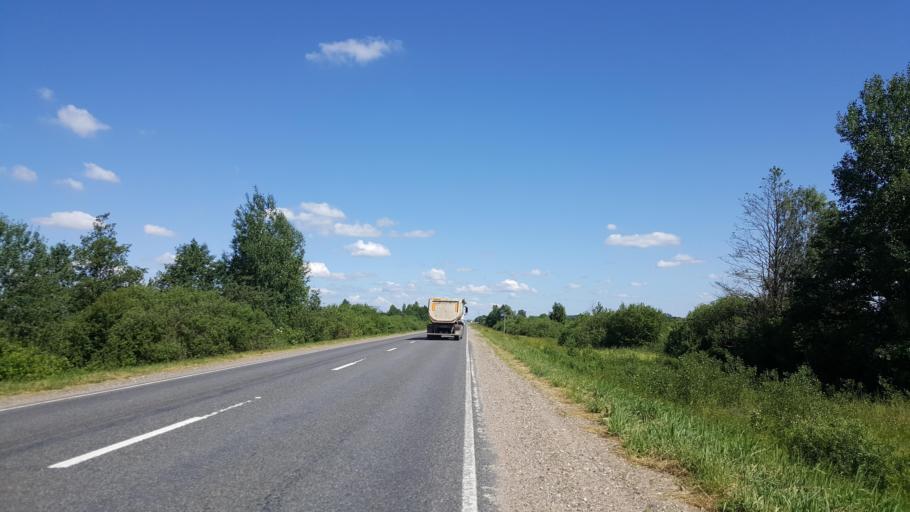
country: BY
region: Brest
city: Kamyanyets
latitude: 52.3896
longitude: 23.7868
